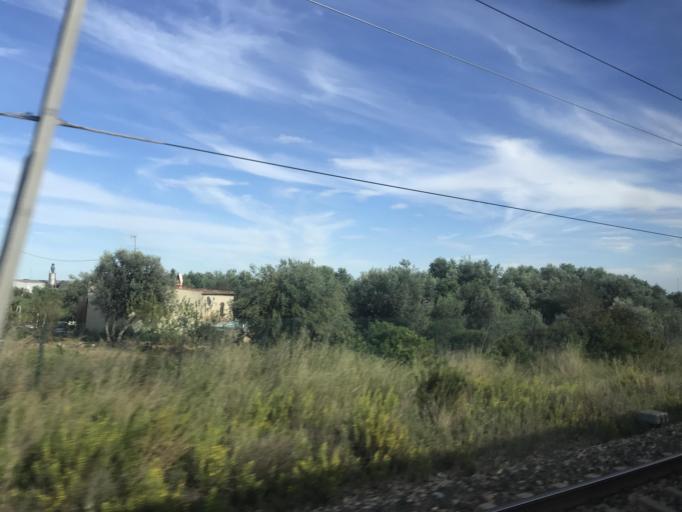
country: ES
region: Valencia
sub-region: Provincia de Castello
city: Vinaros
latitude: 40.4943
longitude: 0.4624
